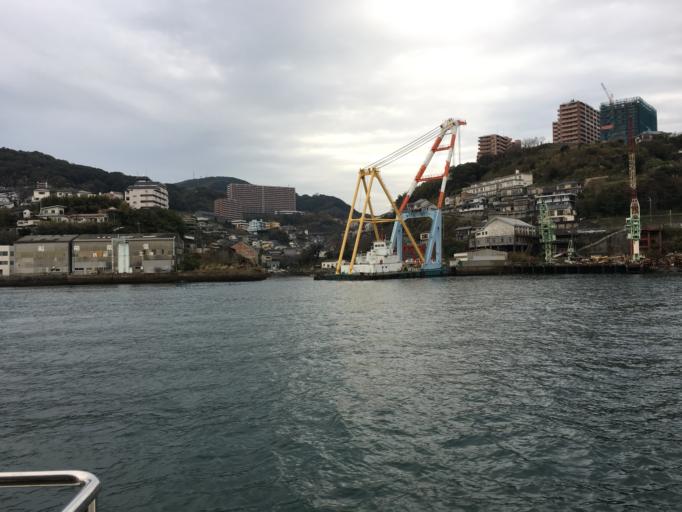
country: JP
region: Nagasaki
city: Nagasaki-shi
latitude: 32.7290
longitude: 129.8585
